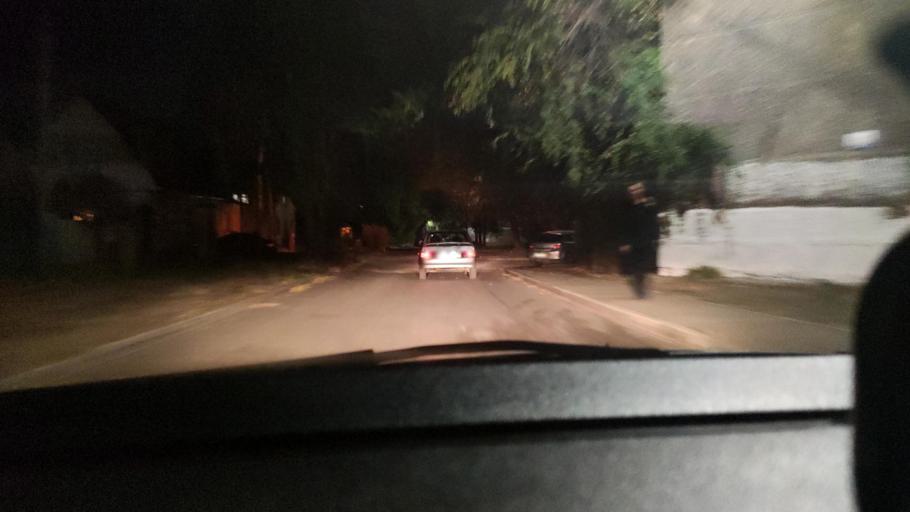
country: RU
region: Voronezj
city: Pridonskoy
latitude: 51.6580
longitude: 39.1218
